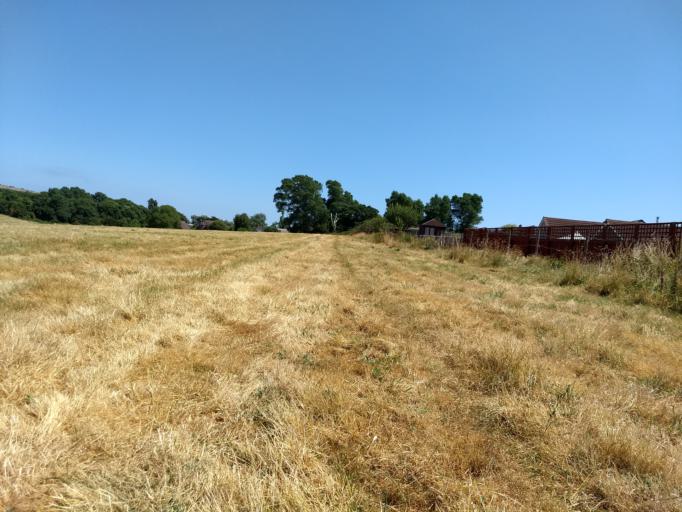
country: GB
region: England
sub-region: Isle of Wight
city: Brading
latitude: 50.6659
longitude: -1.1367
